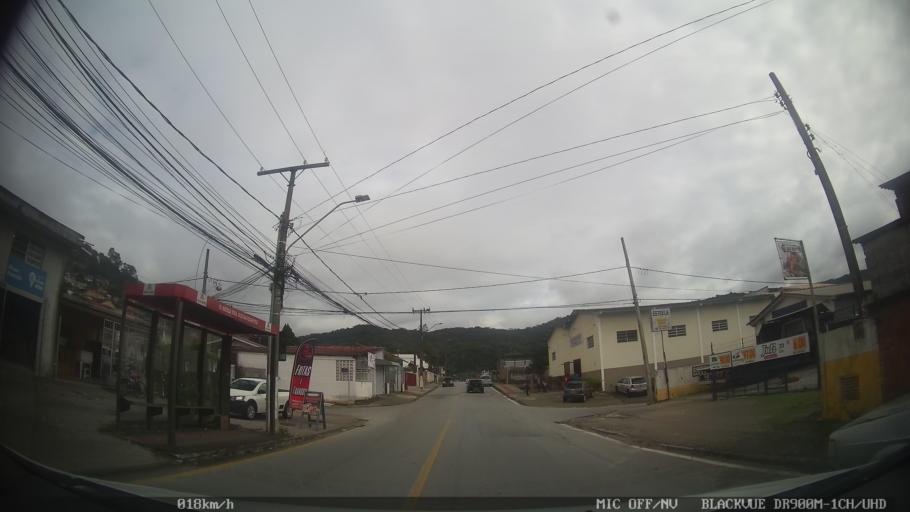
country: BR
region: Santa Catarina
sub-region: Biguacu
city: Biguacu
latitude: -27.5449
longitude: -48.6408
